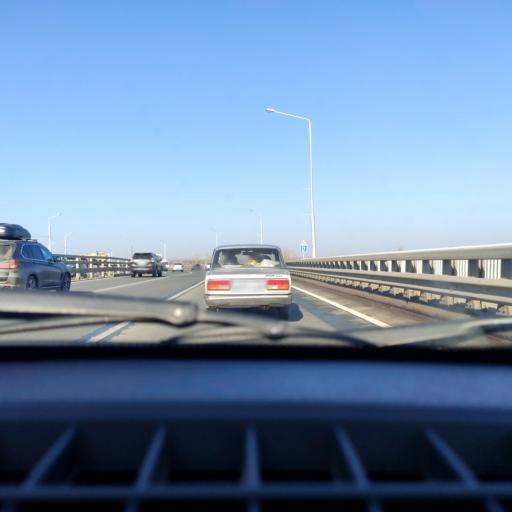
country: RU
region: Bashkortostan
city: Mikhaylovka
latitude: 54.7038
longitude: 55.8581
